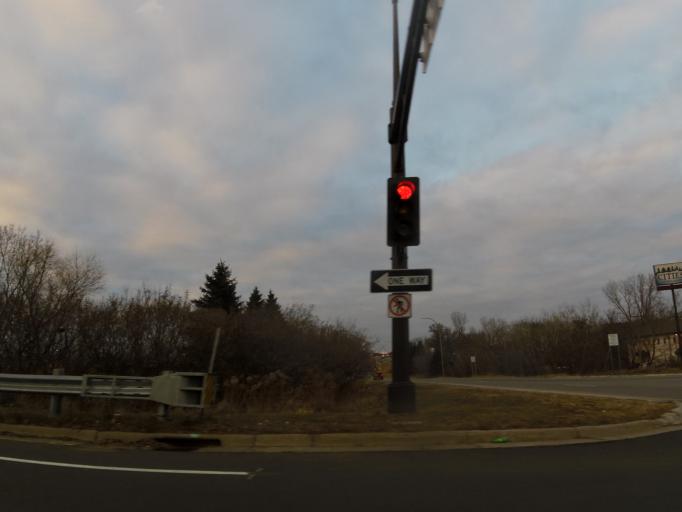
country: US
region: Minnesota
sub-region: Ramsey County
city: Vadnais Heights
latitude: 45.0504
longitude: -93.0577
